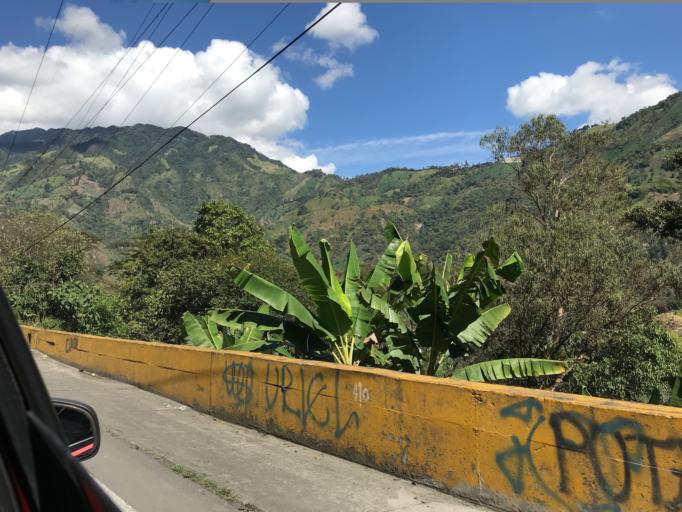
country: CO
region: Tolima
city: Cajamarca
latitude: 4.4399
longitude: -75.4029
